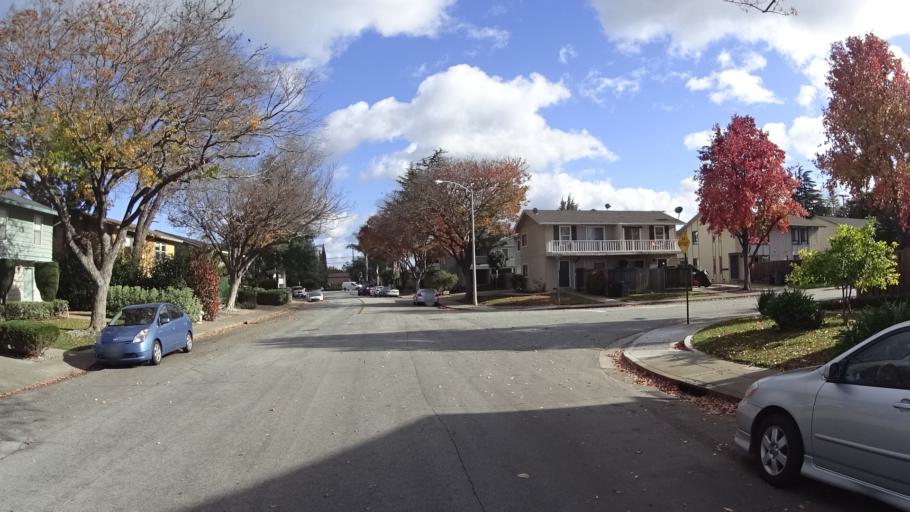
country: US
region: California
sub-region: Santa Clara County
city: Sunnyvale
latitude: 37.3808
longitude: -122.0554
